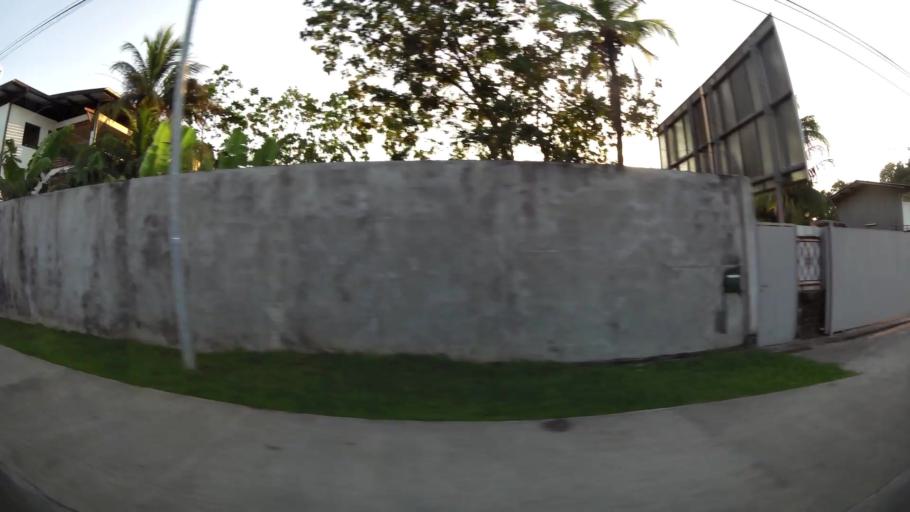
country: GF
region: Guyane
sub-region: Guyane
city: Cayenne
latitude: 4.9298
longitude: -52.3134
